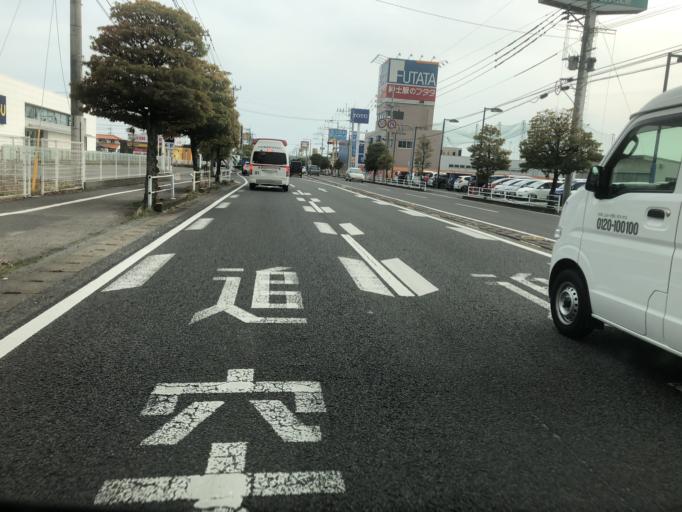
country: JP
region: Saga Prefecture
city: Saga-shi
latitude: 33.2683
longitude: 130.2716
